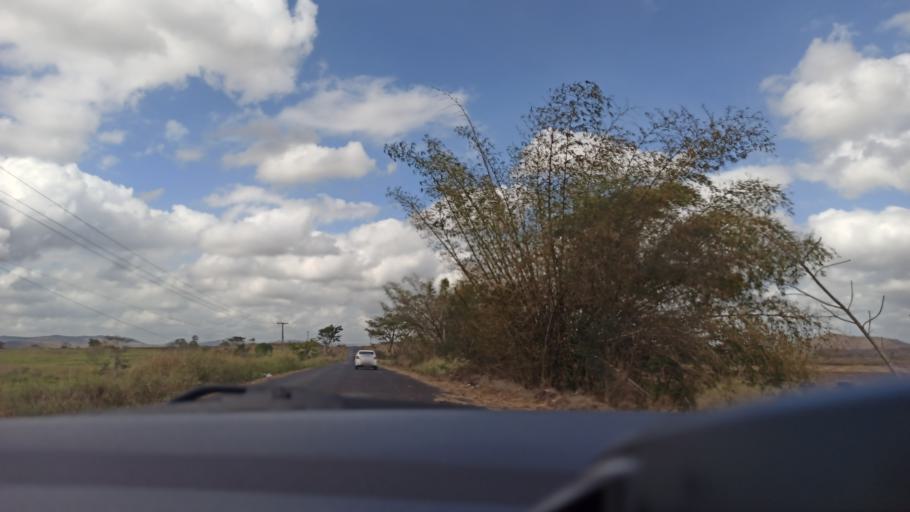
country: BR
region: Pernambuco
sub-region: Timbauba
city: Timbauba
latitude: -7.4756
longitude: -35.2803
